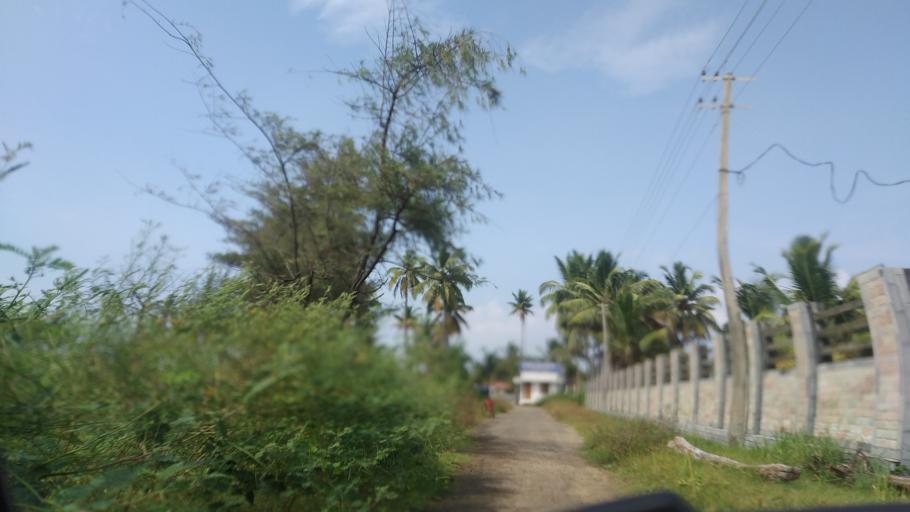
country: IN
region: Kerala
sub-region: Ernakulam
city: Elur
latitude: 10.0829
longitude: 76.1944
